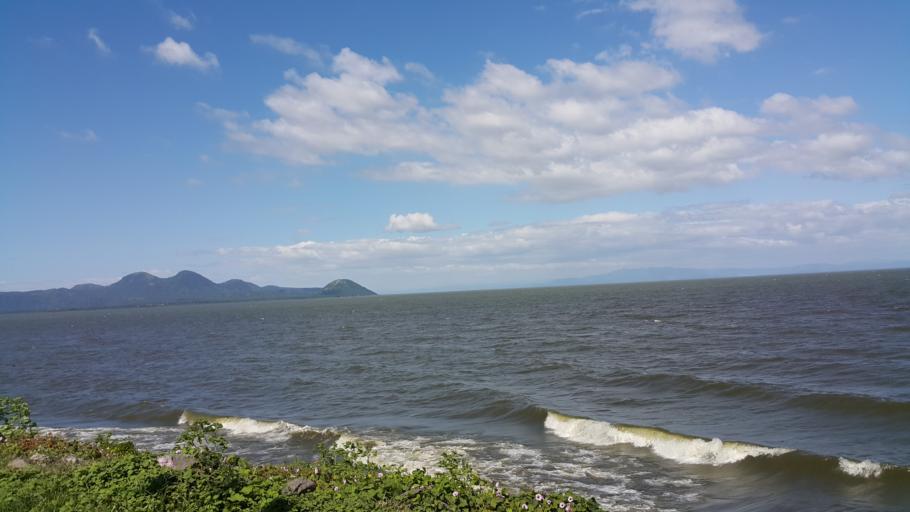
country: NI
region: Managua
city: Managua
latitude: 12.1629
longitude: -86.2764
